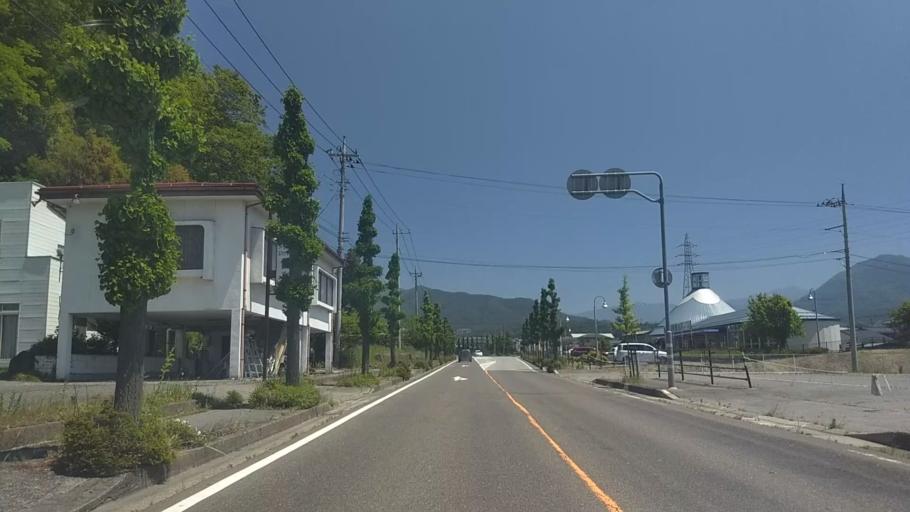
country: JP
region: Yamanashi
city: Nirasaki
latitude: 35.7954
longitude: 138.4224
